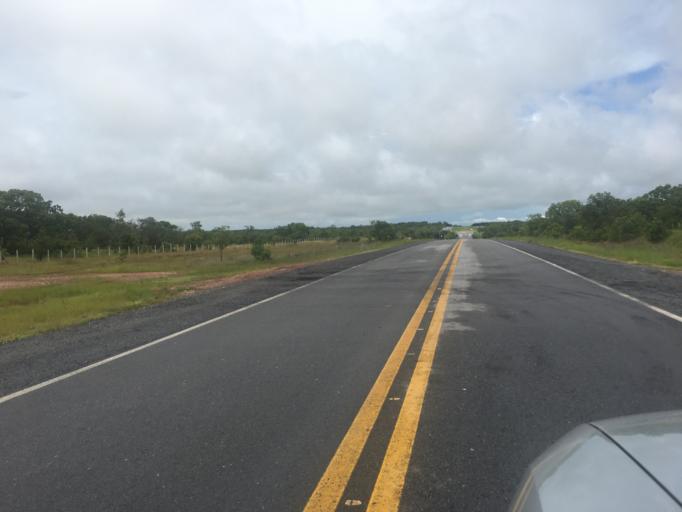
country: BR
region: Goias
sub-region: Campos Belos
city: Campos Belos
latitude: -12.4961
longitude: -47.1929
